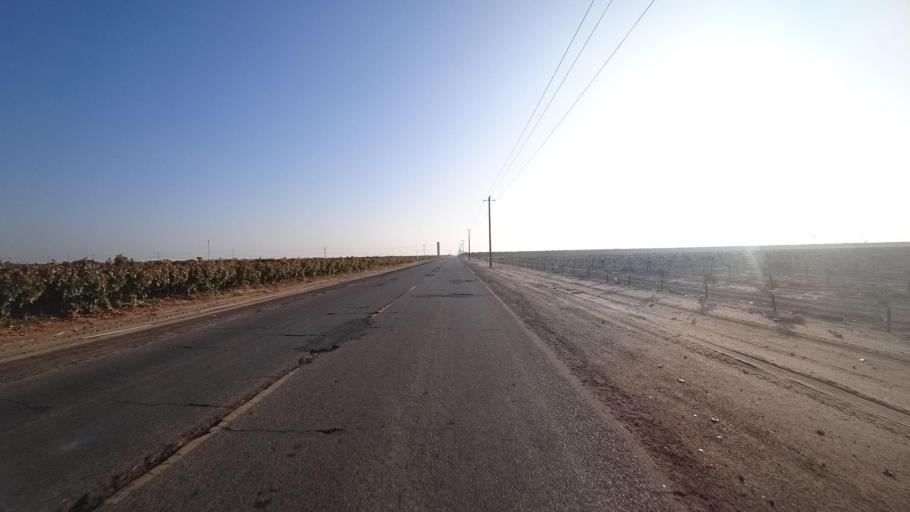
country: US
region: California
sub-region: Tulare County
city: Richgrove
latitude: 35.7906
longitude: -119.1557
